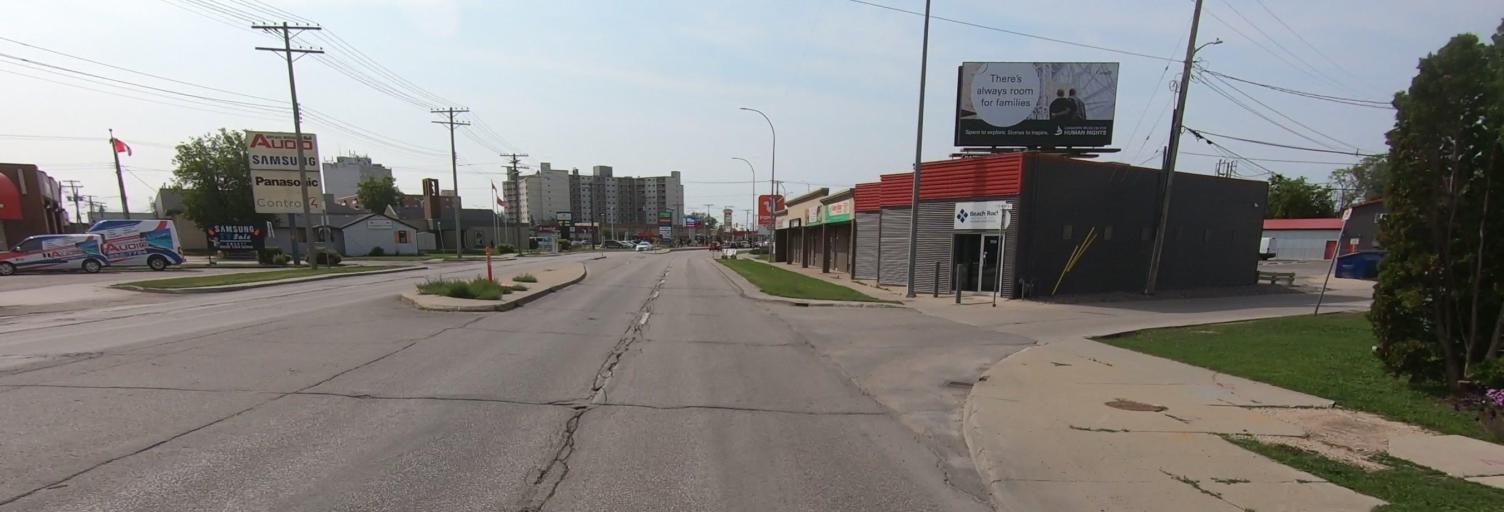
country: CA
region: Manitoba
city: Winnipeg
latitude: 49.8382
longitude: -97.1124
